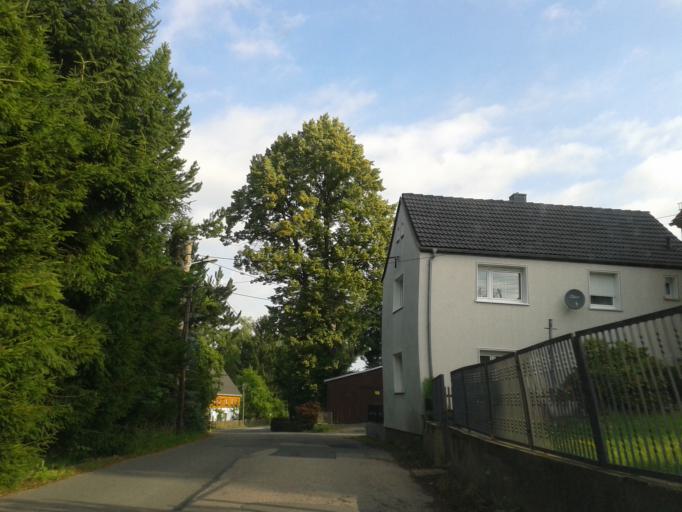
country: DE
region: Saxony
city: Halsbrucke
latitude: 50.9352
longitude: 13.3299
